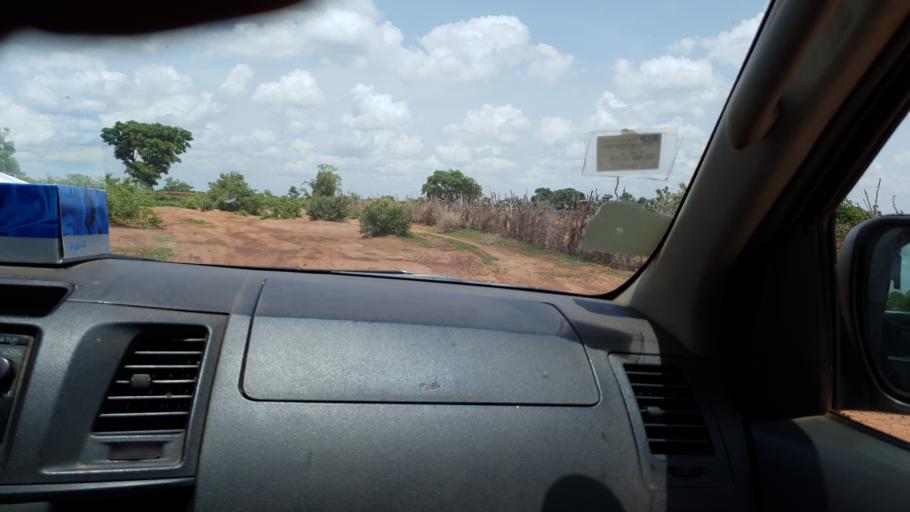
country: ML
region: Koulikoro
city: Banamba
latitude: 13.3770
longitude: -7.2176
